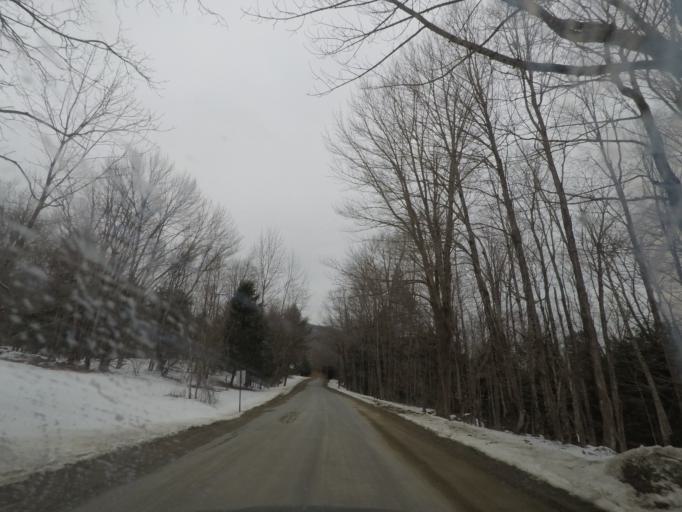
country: US
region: New York
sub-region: Rensselaer County
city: Averill Park
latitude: 42.5460
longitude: -73.4120
